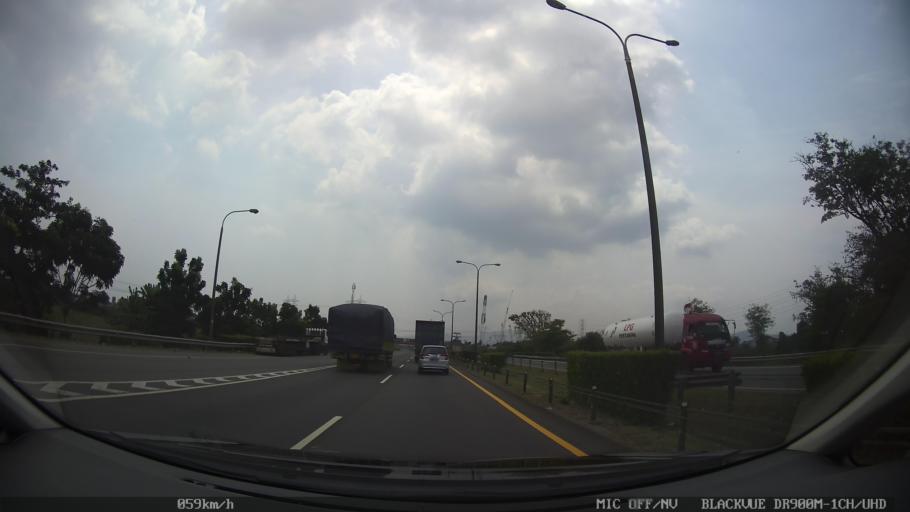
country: ID
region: Banten
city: Bojonegara
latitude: -6.0196
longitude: 106.0899
